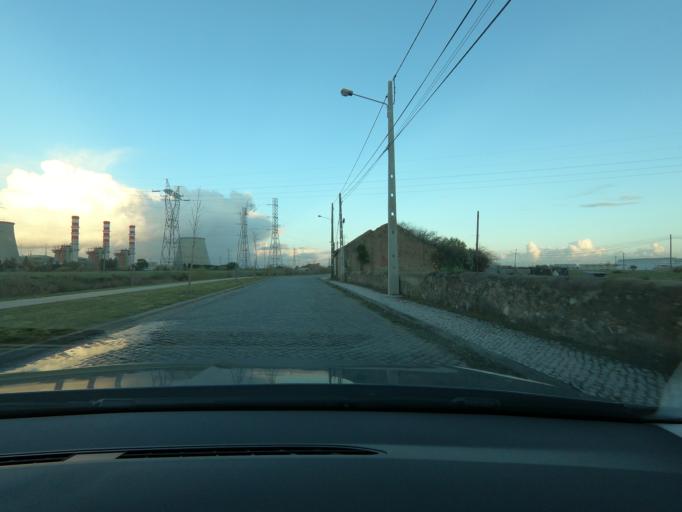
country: PT
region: Lisbon
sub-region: Alenquer
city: Carregado
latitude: 39.0107
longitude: -8.9596
